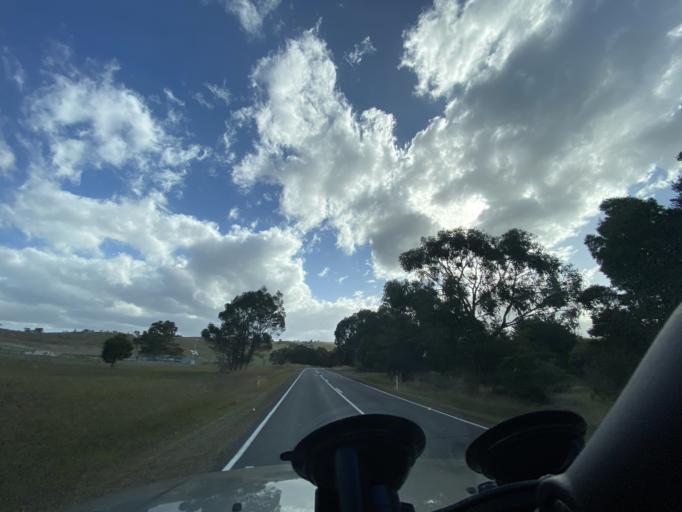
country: AU
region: Victoria
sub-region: Murrindindi
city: Kinglake West
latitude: -37.3223
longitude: 145.3041
